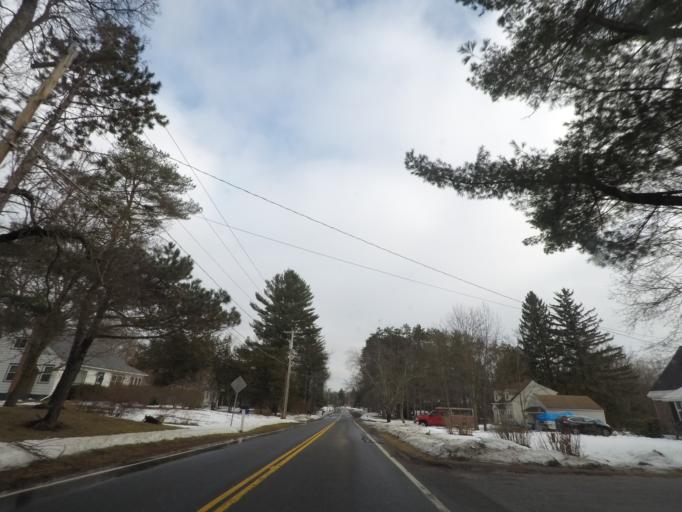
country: US
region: New York
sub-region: Schenectady County
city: Rotterdam
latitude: 42.7261
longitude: -73.9448
